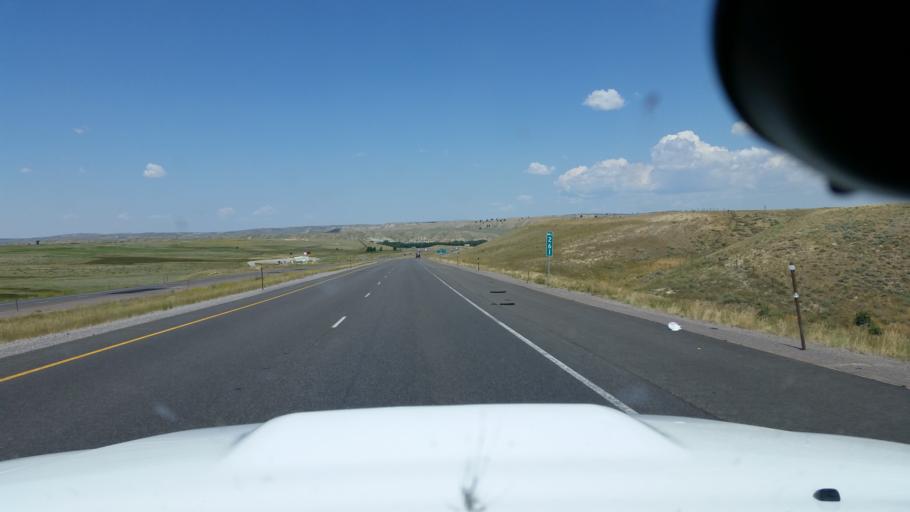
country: US
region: Wyoming
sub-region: Carbon County
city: Saratoga
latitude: 41.6830
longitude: -106.3773
